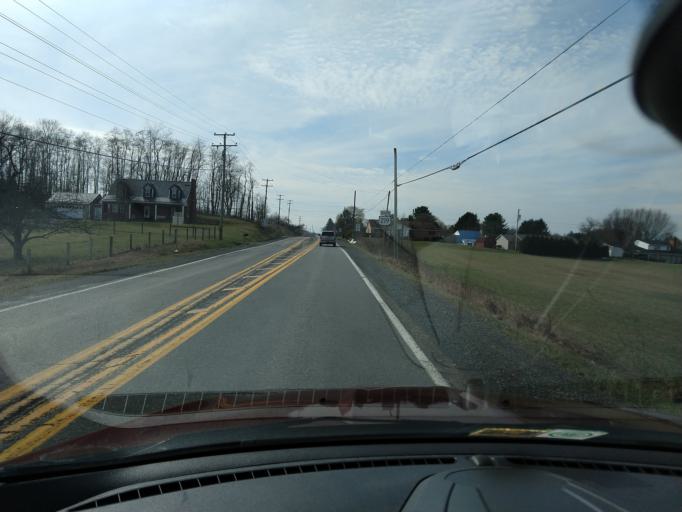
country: US
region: West Virginia
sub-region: Greenbrier County
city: Lewisburg
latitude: 37.8480
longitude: -80.4142
